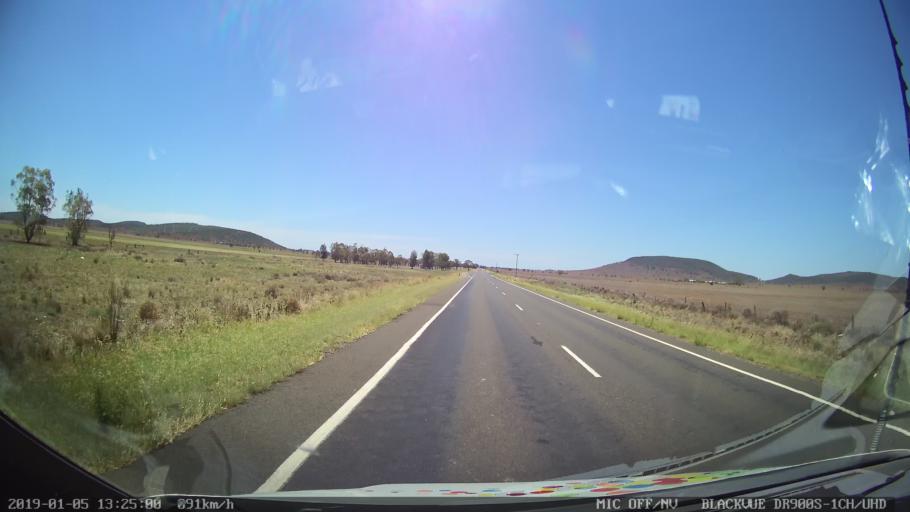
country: AU
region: New South Wales
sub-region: Gunnedah
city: Gunnedah
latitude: -31.0649
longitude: 149.9964
